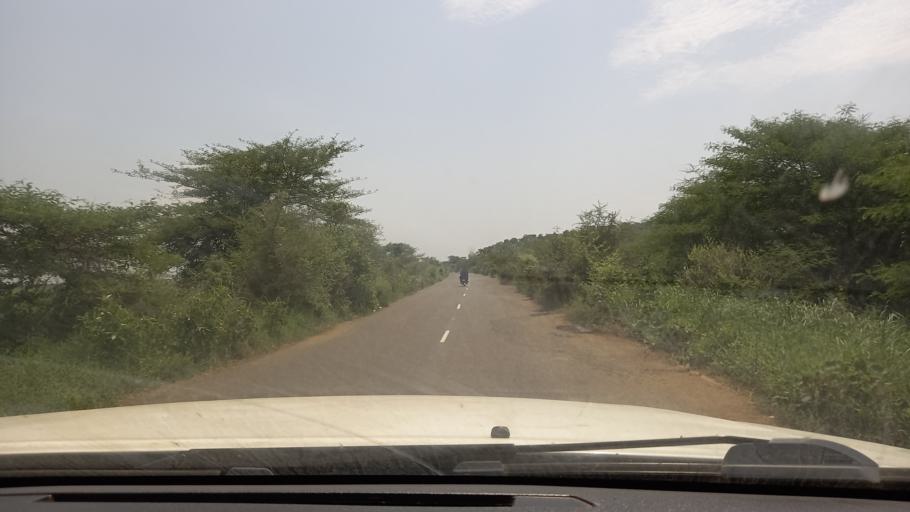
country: ET
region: Gambela
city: Gambela
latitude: 8.2828
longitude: 34.2193
